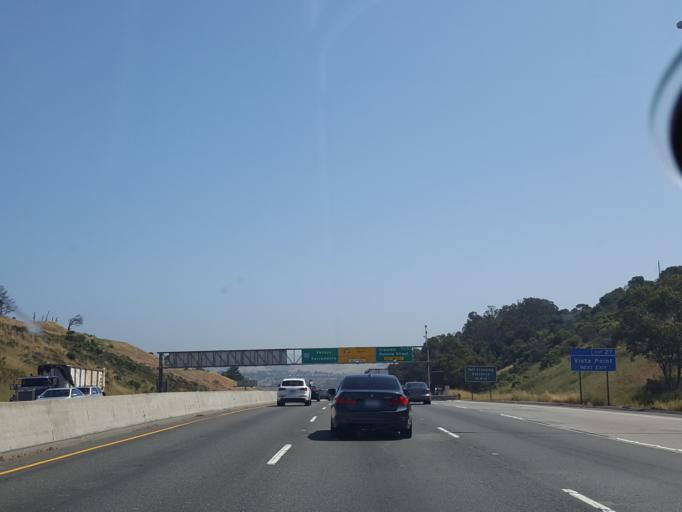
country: US
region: California
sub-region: Contra Costa County
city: Crockett
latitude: 38.0483
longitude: -122.2335
